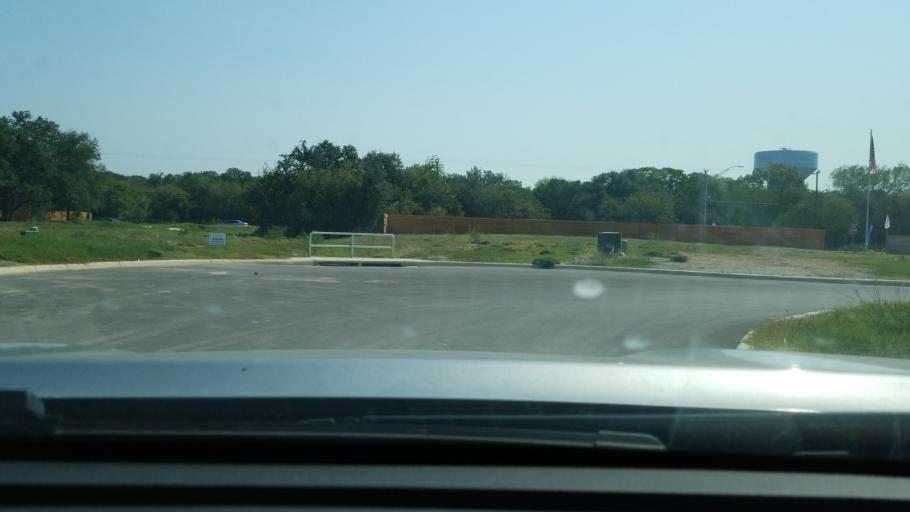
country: US
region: Texas
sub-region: Bexar County
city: Leon Valley
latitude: 29.5456
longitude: -98.6117
